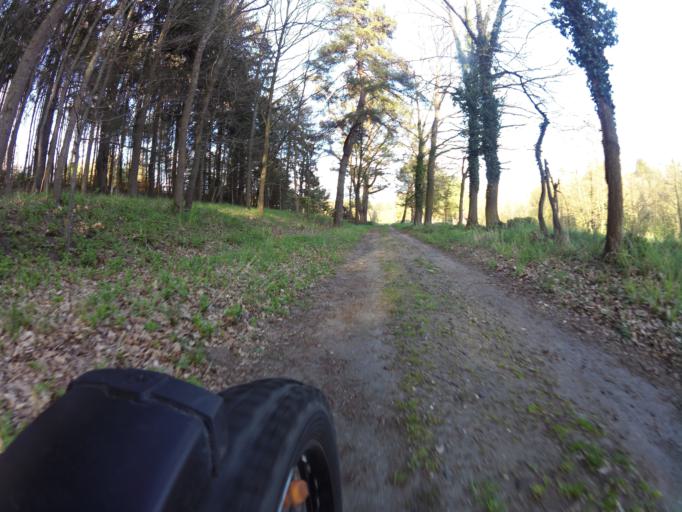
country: PL
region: West Pomeranian Voivodeship
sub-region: Powiat gryficki
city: Ploty
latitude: 53.7419
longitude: 15.2699
